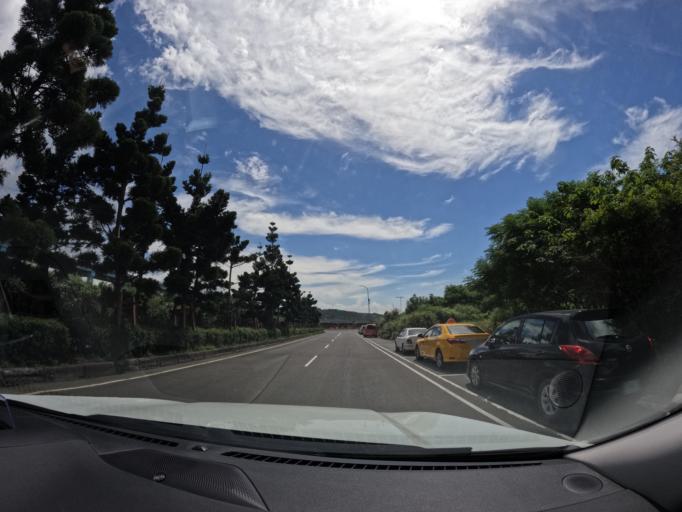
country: TW
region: Taipei
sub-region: Taipei
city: Banqiao
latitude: 25.1500
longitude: 121.3905
